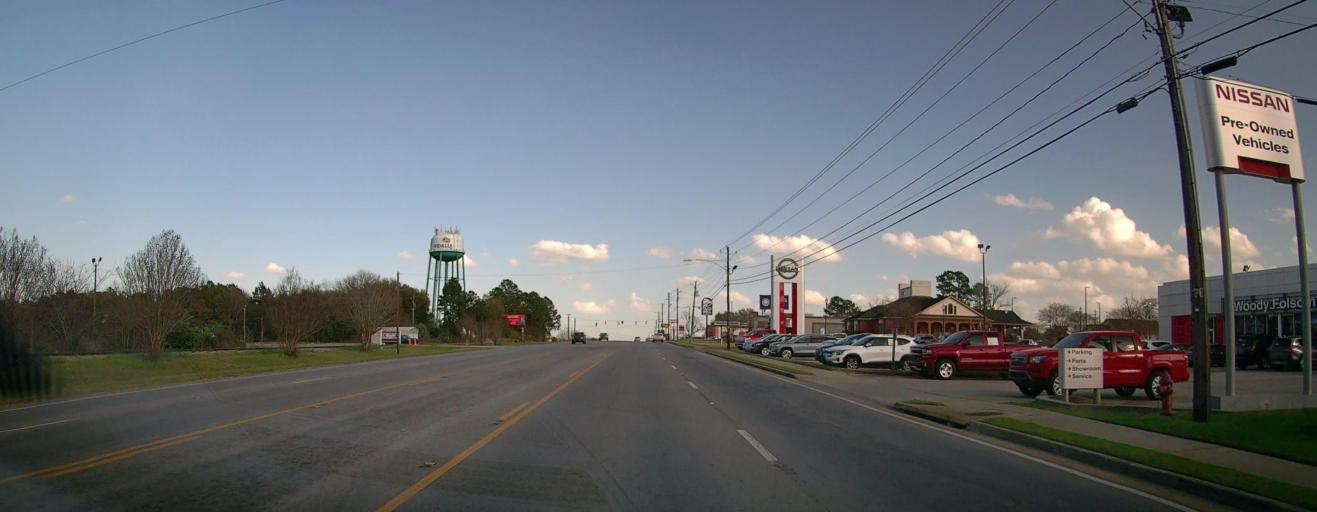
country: US
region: Georgia
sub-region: Toombs County
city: Vidalia
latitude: 32.2112
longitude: -82.3919
